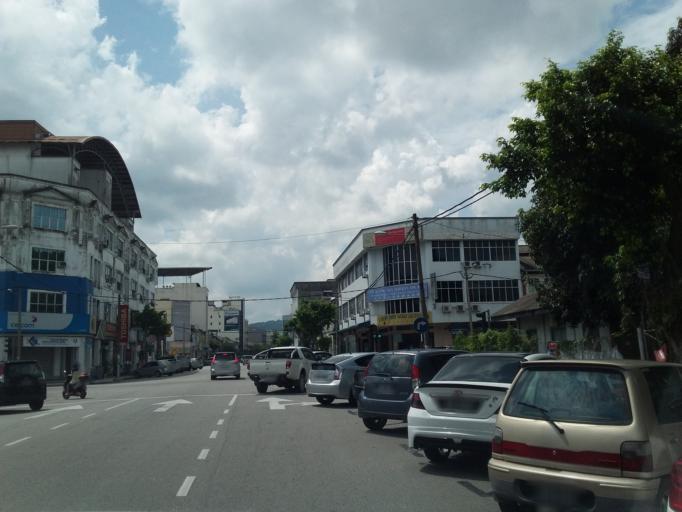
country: MY
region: Johor
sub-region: Daerah Batu Pahat
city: Batu Pahat
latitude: 1.8516
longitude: 102.9256
